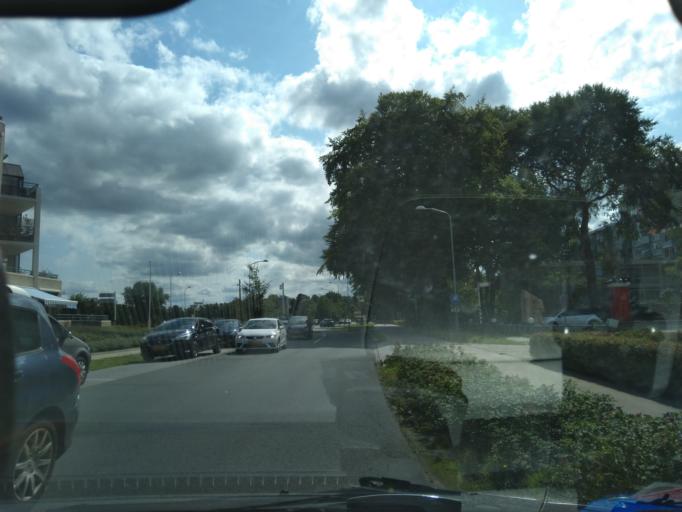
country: NL
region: Groningen
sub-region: Gemeente Haren
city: Haren
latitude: 53.1583
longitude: 6.5633
